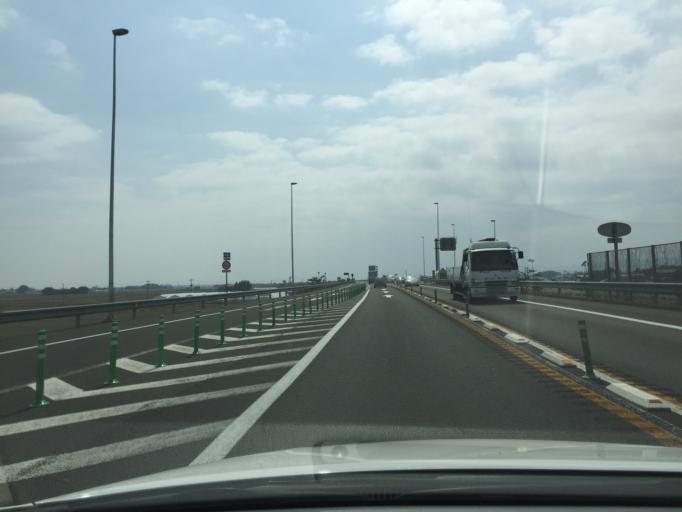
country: JP
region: Miyagi
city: Iwanuma
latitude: 38.0863
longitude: 140.8868
